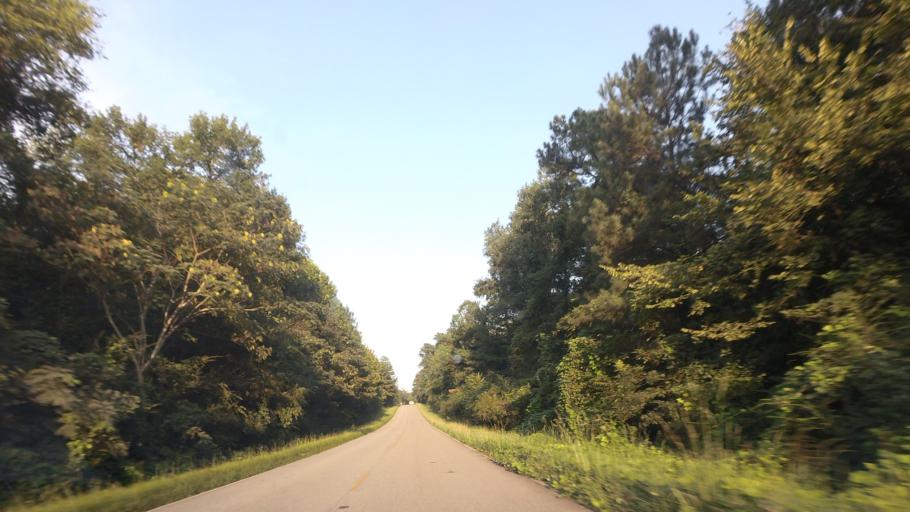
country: US
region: Georgia
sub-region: Bibb County
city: West Point
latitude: 32.8972
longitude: -83.8191
